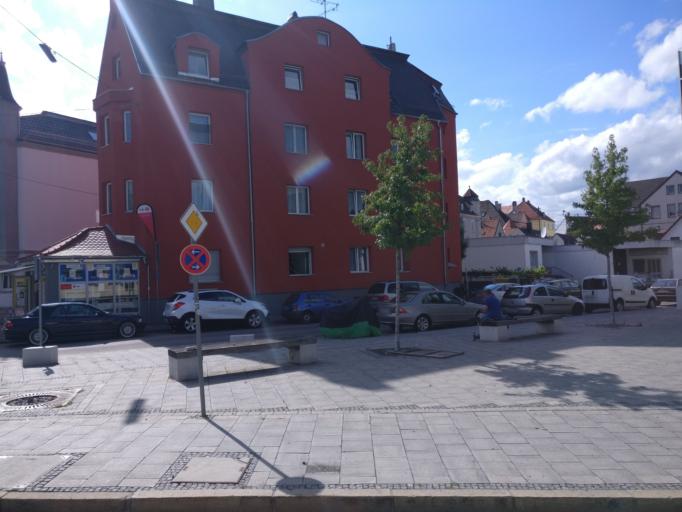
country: DE
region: Bavaria
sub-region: Swabia
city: Augsburg
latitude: 48.3830
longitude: 10.8803
